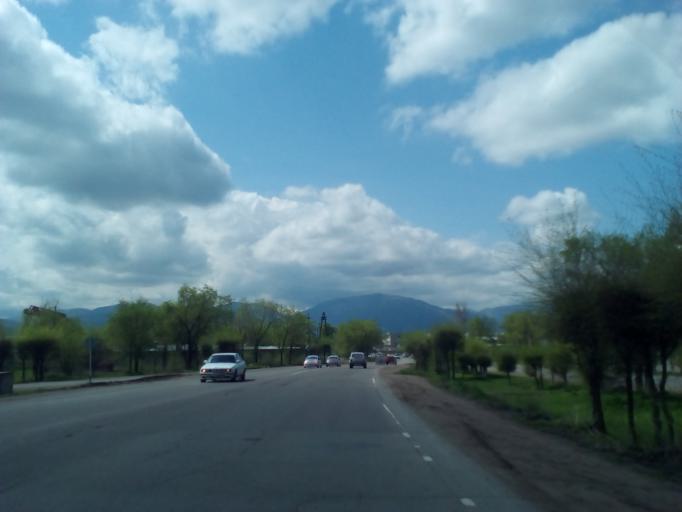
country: KZ
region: Almaty Oblysy
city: Burunday
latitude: 43.2165
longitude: 76.6468
